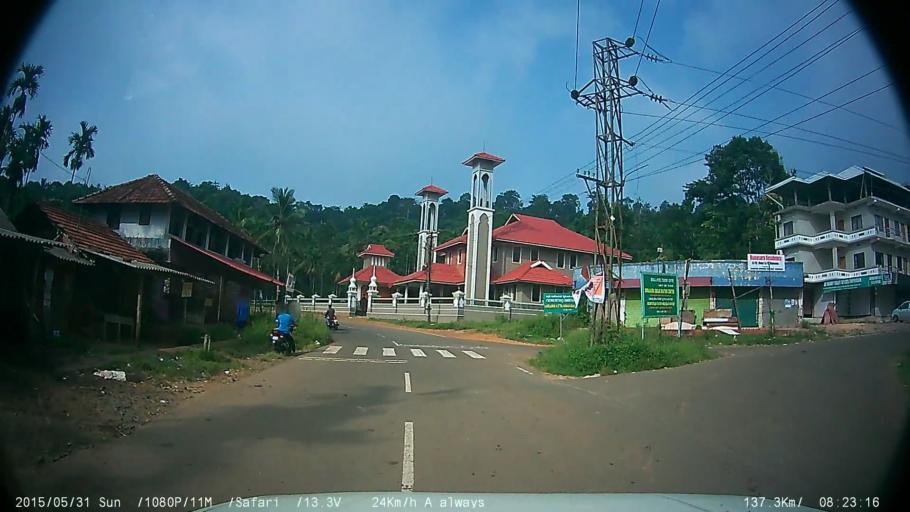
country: IN
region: Kerala
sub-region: Wayanad
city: Kalpetta
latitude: 11.6733
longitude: 75.9704
